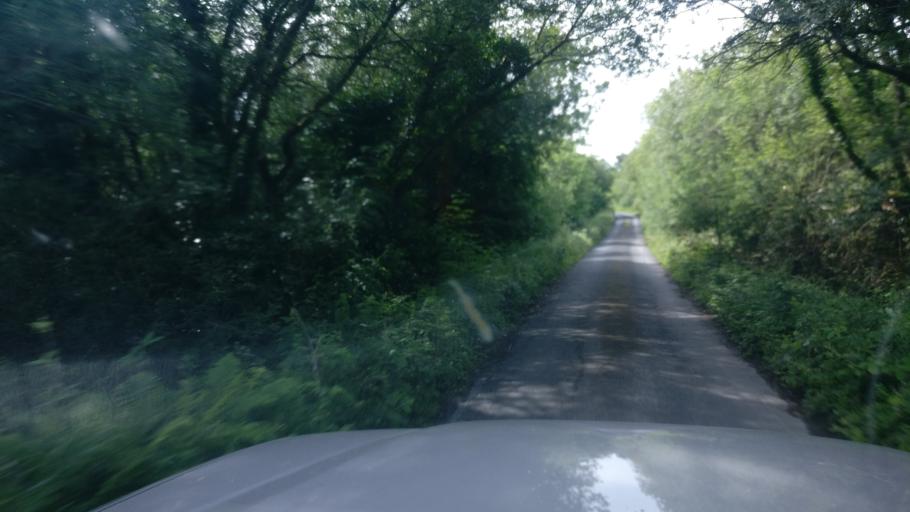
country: IE
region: Connaught
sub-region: County Galway
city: Gort
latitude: 53.0996
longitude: -8.7004
